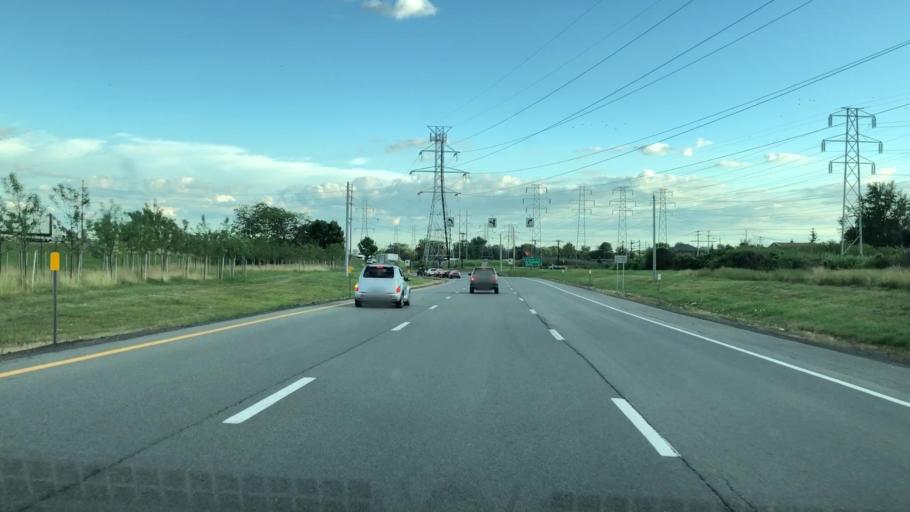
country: US
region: New York
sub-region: Erie County
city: Cheektowaga
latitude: 42.8859
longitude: -78.7684
